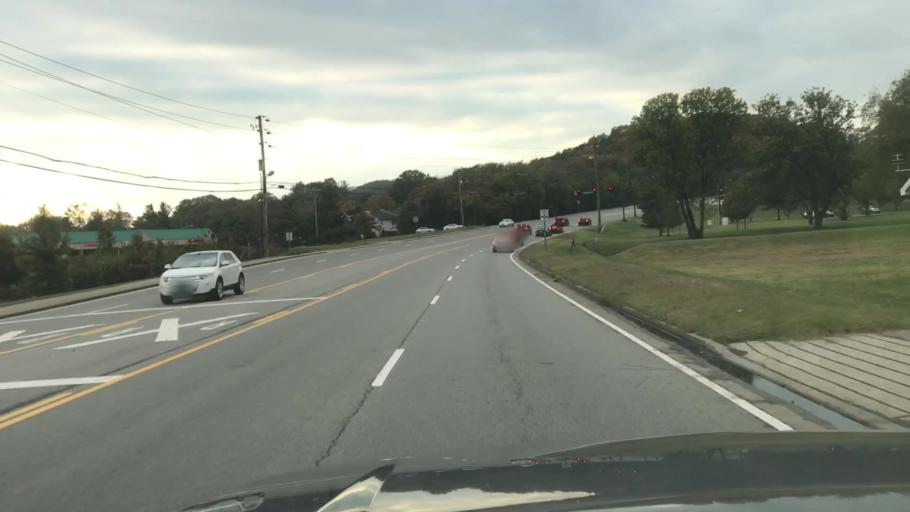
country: US
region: Tennessee
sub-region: Williamson County
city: Franklin
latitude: 35.9676
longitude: -86.8164
